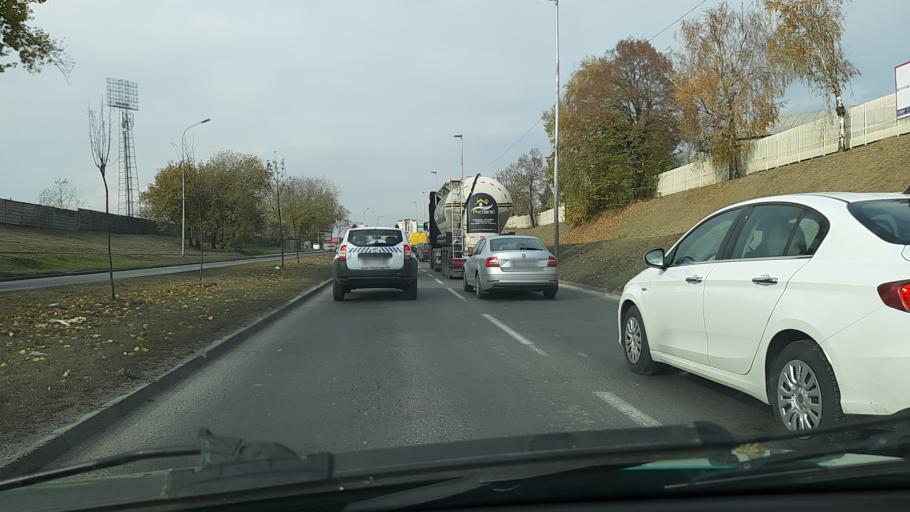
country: MK
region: Cair
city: Cair
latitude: 41.9985
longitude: 21.4745
